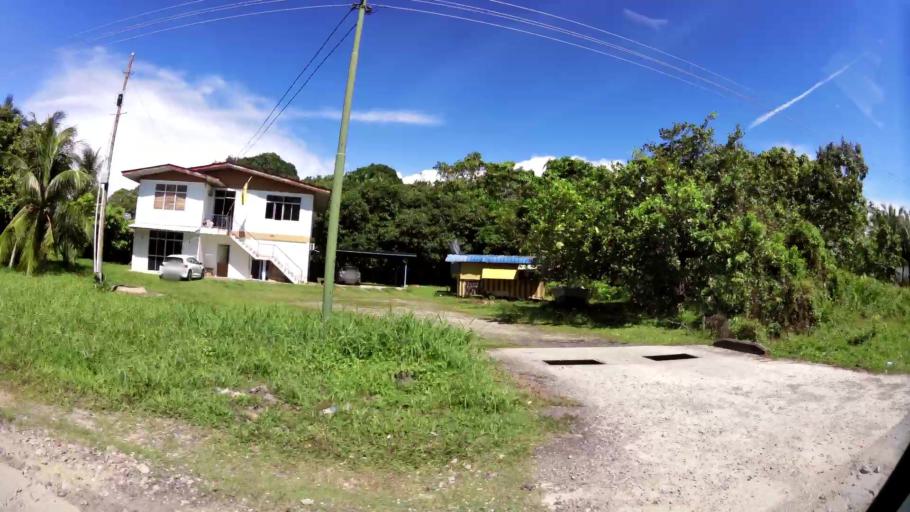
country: BN
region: Brunei and Muara
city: Bandar Seri Begawan
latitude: 5.0081
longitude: 115.0591
